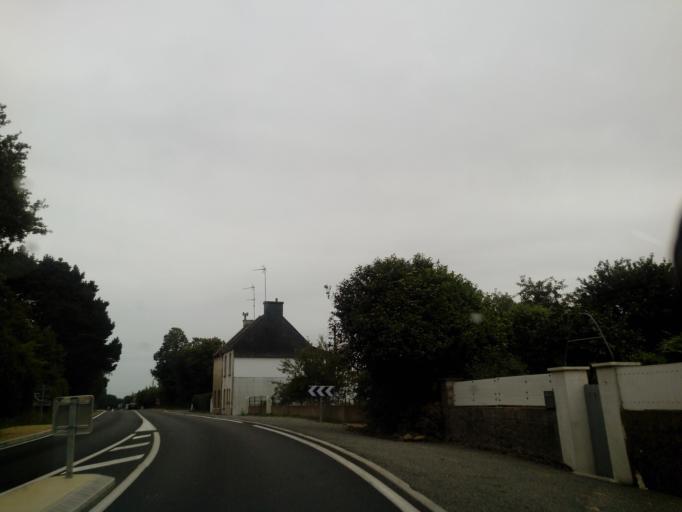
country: FR
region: Brittany
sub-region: Departement du Finistere
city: Quimperle
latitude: 47.8587
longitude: -3.5171
